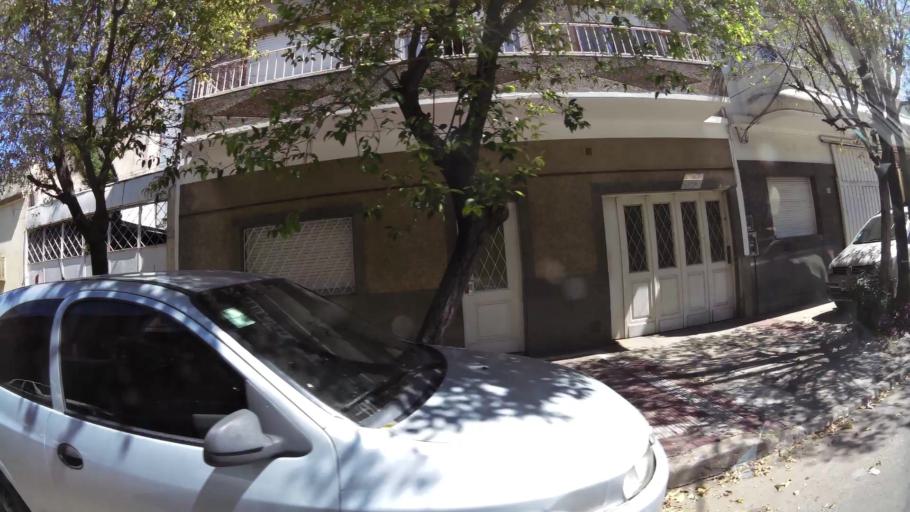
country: AR
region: Buenos Aires
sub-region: Partido de General San Martin
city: General San Martin
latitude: -34.5834
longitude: -58.5280
